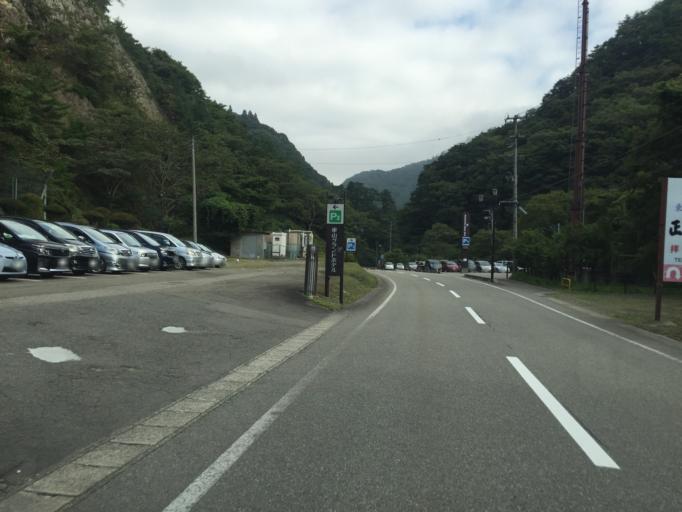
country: JP
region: Fukushima
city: Inawashiro
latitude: 37.4696
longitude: 139.9627
